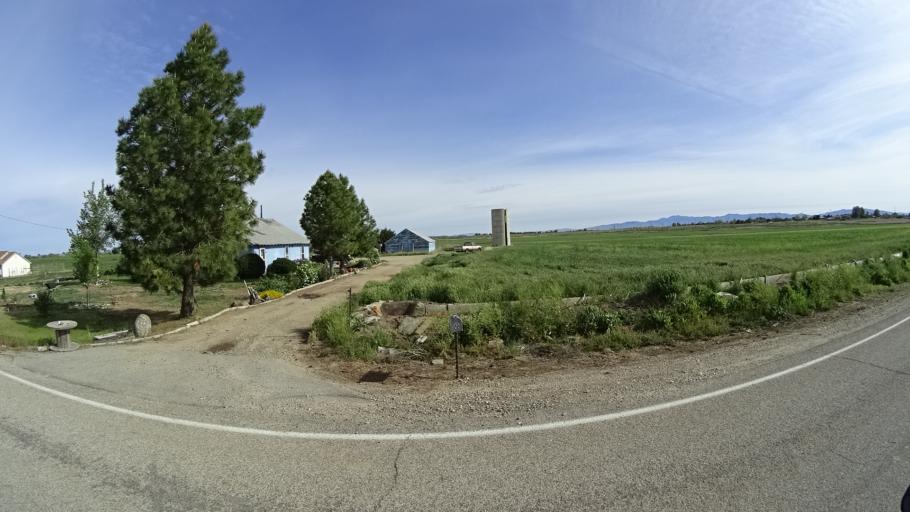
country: US
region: Idaho
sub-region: Ada County
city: Kuna
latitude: 43.4735
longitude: -116.3432
